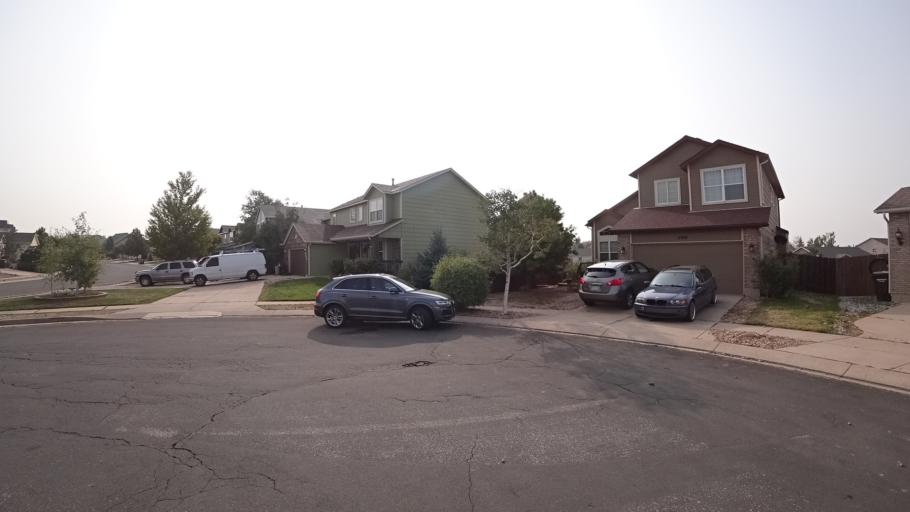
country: US
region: Colorado
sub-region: El Paso County
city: Cimarron Hills
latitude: 38.9342
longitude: -104.7374
